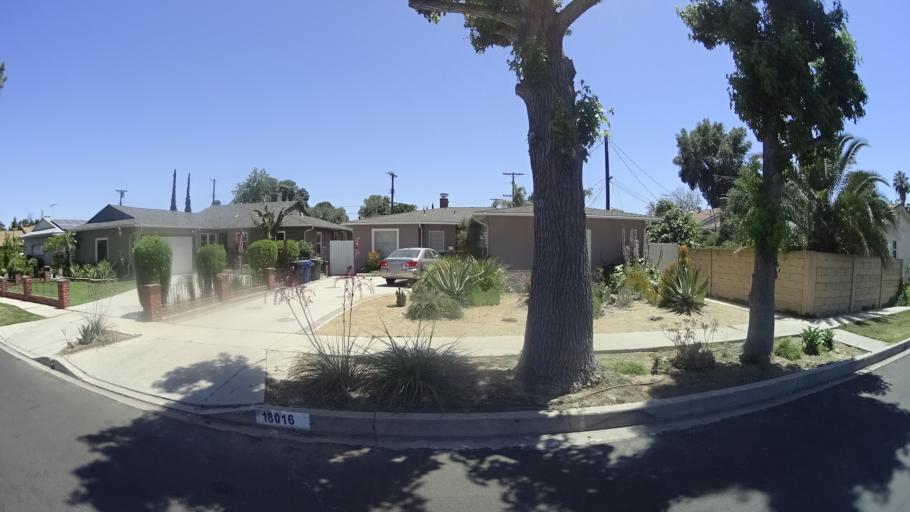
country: US
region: California
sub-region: Los Angeles County
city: Northridge
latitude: 34.1929
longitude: -118.5257
